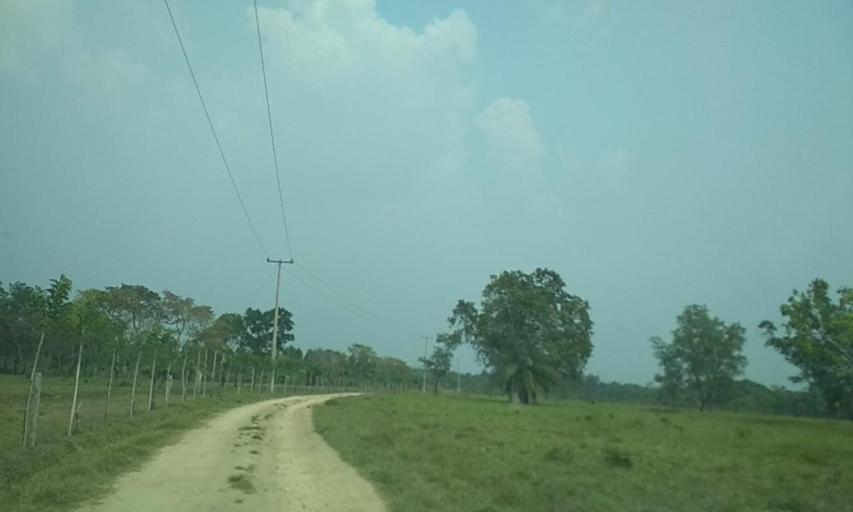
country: MX
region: Veracruz
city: Las Choapas
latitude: 17.8177
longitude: -94.0661
